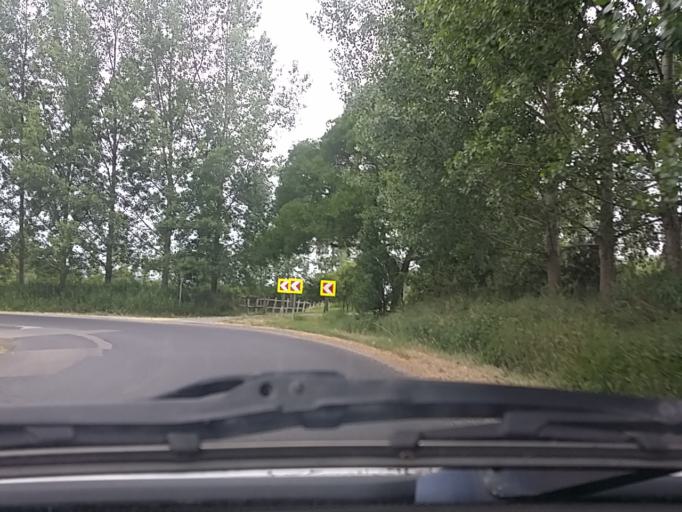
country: HU
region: Pest
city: Pilisvorosvar
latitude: 47.6300
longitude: 18.9347
